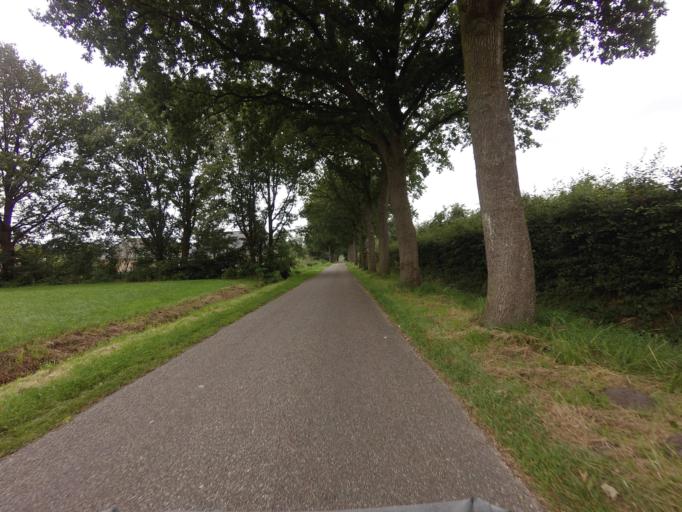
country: NL
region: Overijssel
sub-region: Gemeente Steenwijkerland
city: Tuk
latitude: 52.8272
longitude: 6.0867
